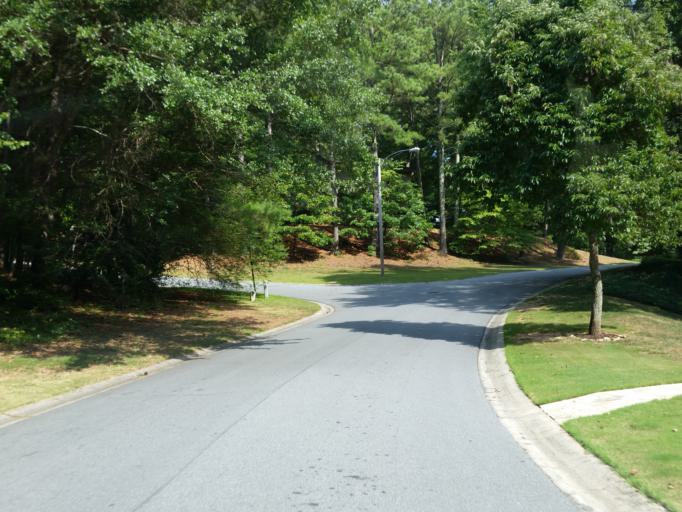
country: US
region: Georgia
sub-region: Fulton County
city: Roswell
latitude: 34.0476
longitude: -84.4264
